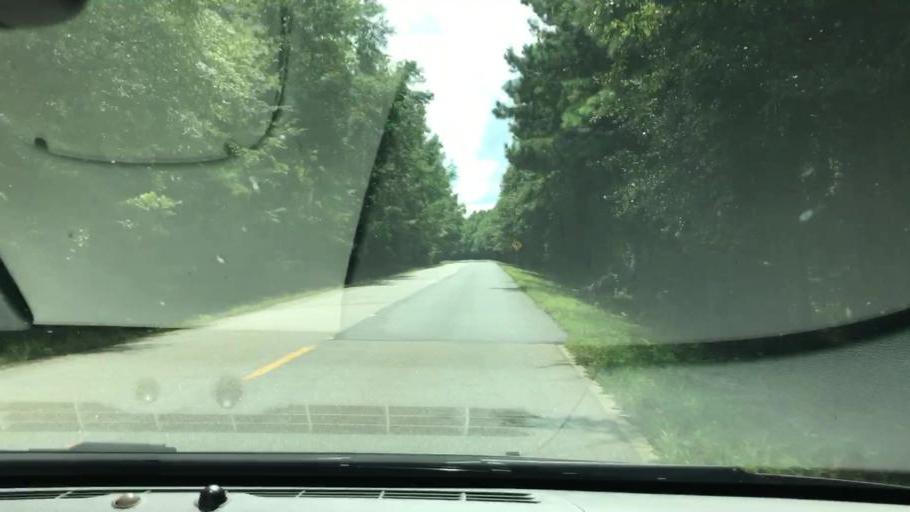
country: US
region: Georgia
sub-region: Quitman County
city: Georgetown
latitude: 31.9885
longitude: -85.0478
